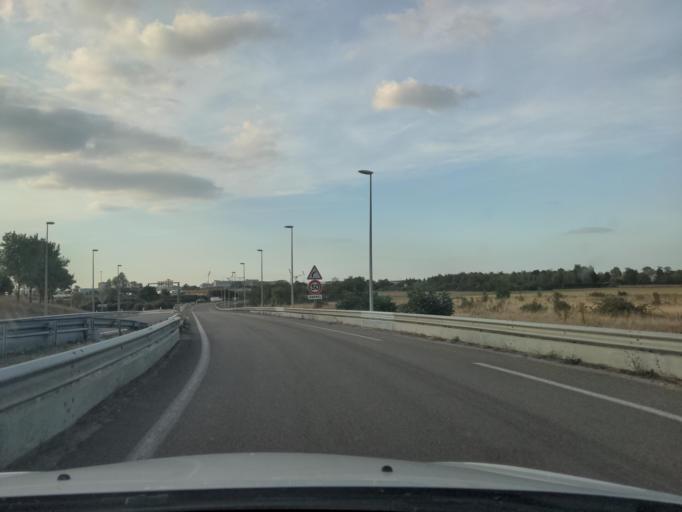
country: FR
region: Bourgogne
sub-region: Departement de la Cote-d'Or
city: Longvic
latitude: 47.3032
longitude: 5.0785
